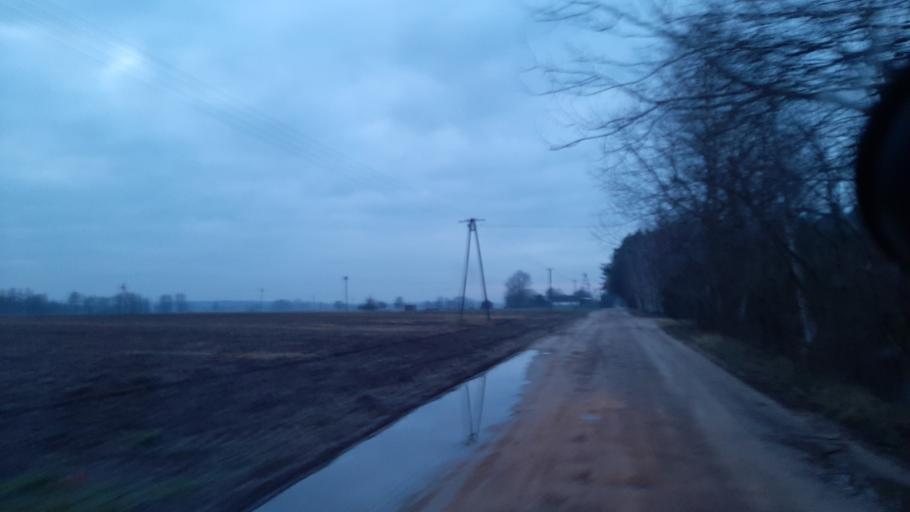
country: PL
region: Lublin Voivodeship
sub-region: Powiat lubartowski
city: Firlej
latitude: 51.5884
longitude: 22.5373
